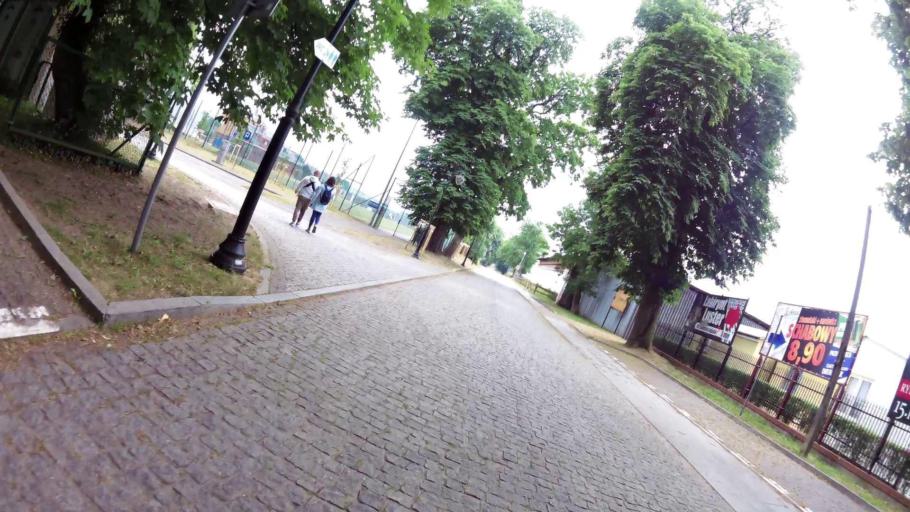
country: PL
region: West Pomeranian Voivodeship
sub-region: Powiat gryficki
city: Rewal
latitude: 54.0743
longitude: 14.9934
